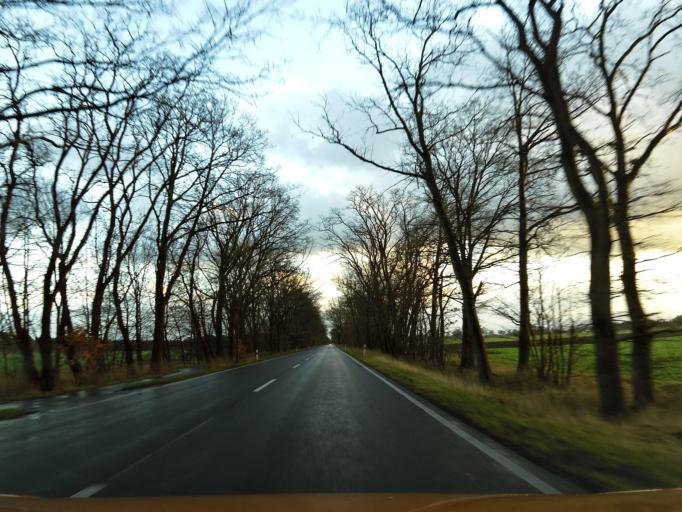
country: DE
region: Lower Saxony
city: Meinersen
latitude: 52.4289
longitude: 10.3366
